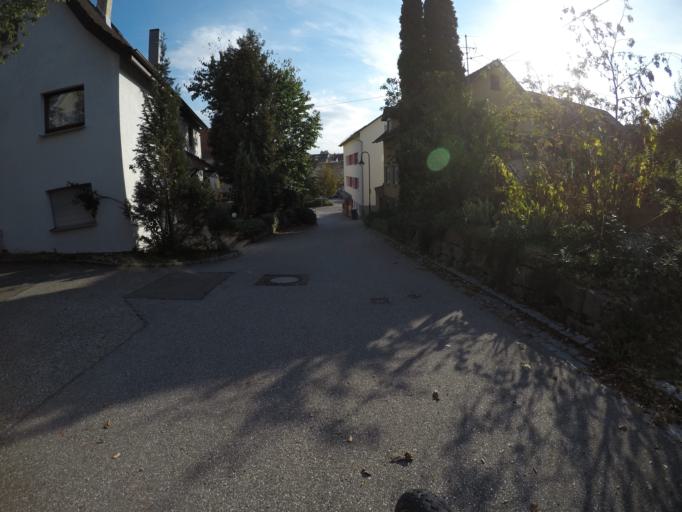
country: DE
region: Baden-Wuerttemberg
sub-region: Tuebingen Region
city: Sickenhausen
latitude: 48.5336
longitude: 9.2014
